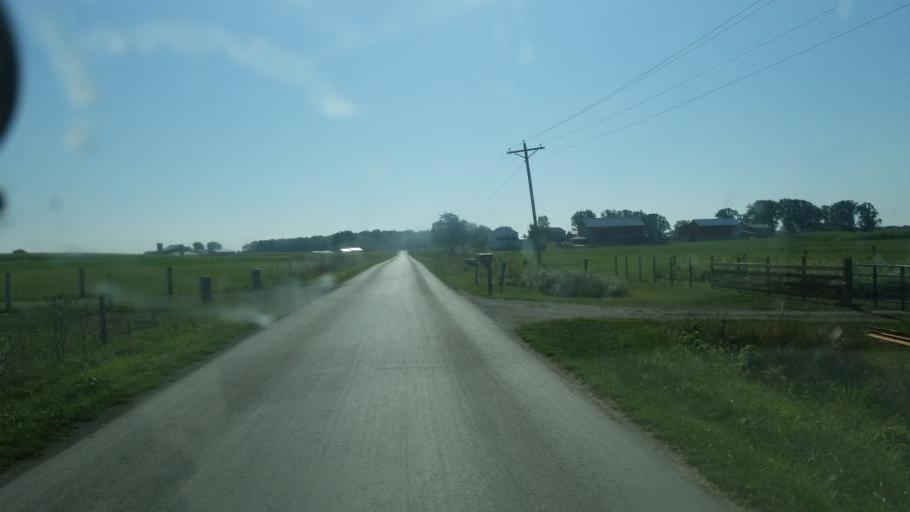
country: US
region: Ohio
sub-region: Hardin County
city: Kenton
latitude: 40.5653
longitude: -83.4473
